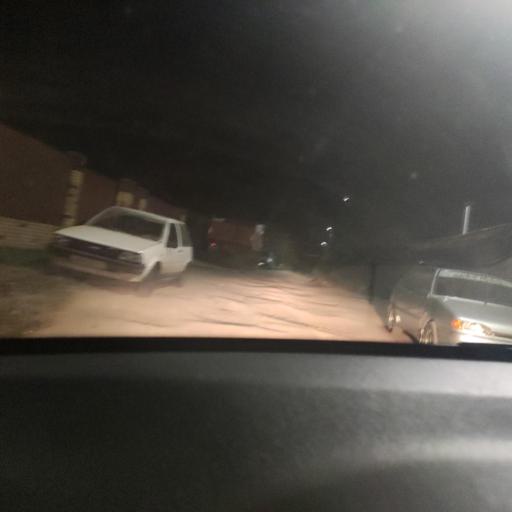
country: RU
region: Samara
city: Samara
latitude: 53.2221
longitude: 50.2228
